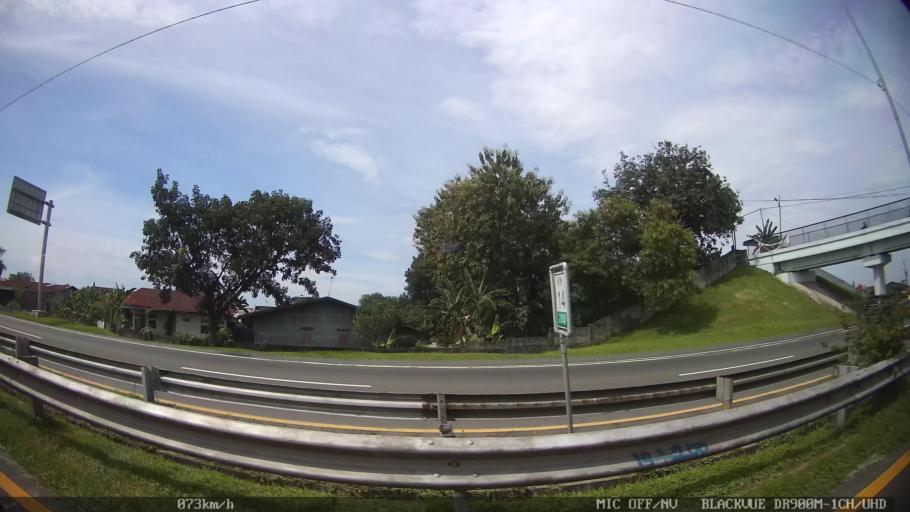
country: ID
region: North Sumatra
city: Medan
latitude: 3.6471
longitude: 98.6856
